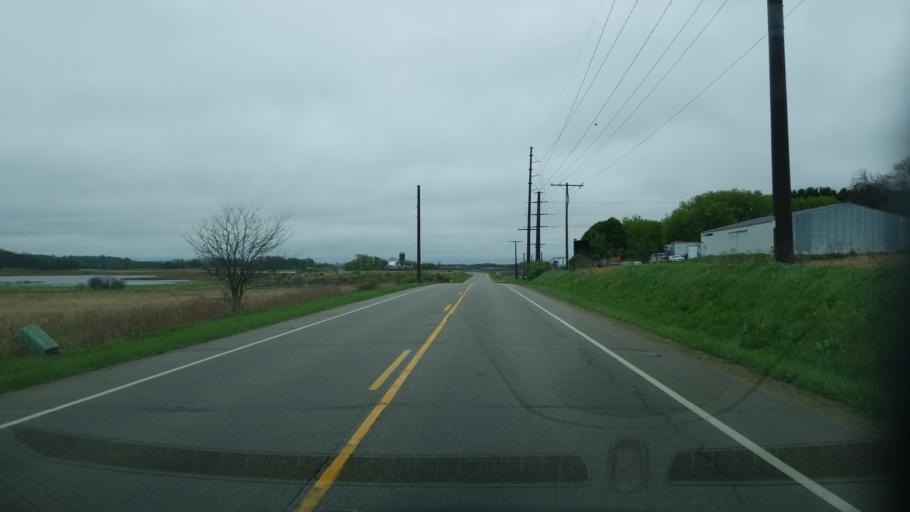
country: US
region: Wisconsin
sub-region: Dane County
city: Fitchburg
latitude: 42.9666
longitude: -89.4351
